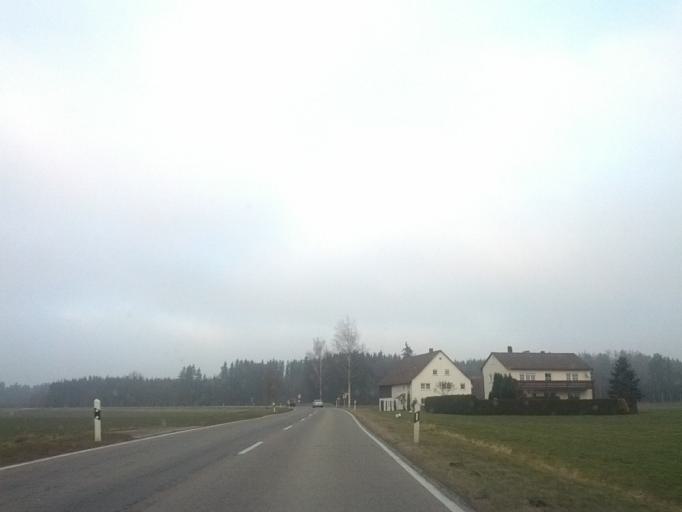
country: DE
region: Baden-Wuerttemberg
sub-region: Tuebingen Region
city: Bad Wurzach
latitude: 47.9491
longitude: 9.9395
